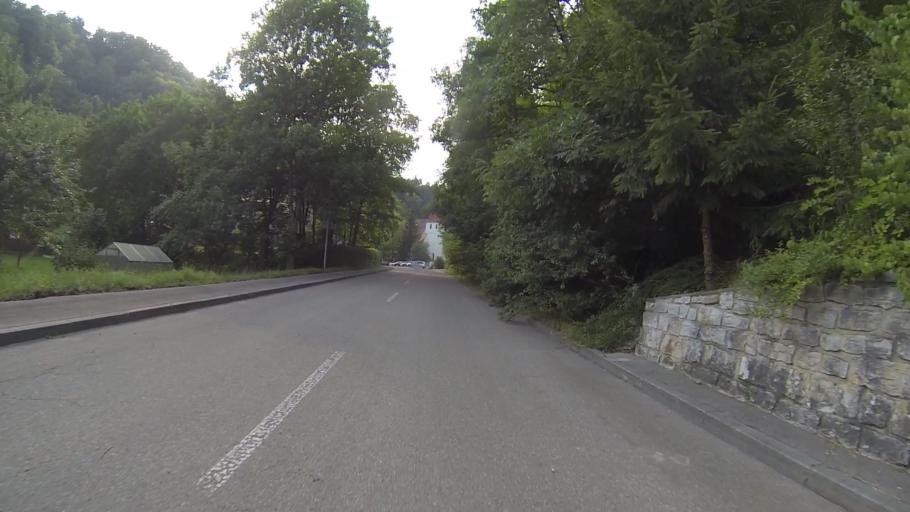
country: DE
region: Baden-Wuerttemberg
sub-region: Tuebingen Region
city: Dornstadt
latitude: 48.4462
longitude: 9.8632
